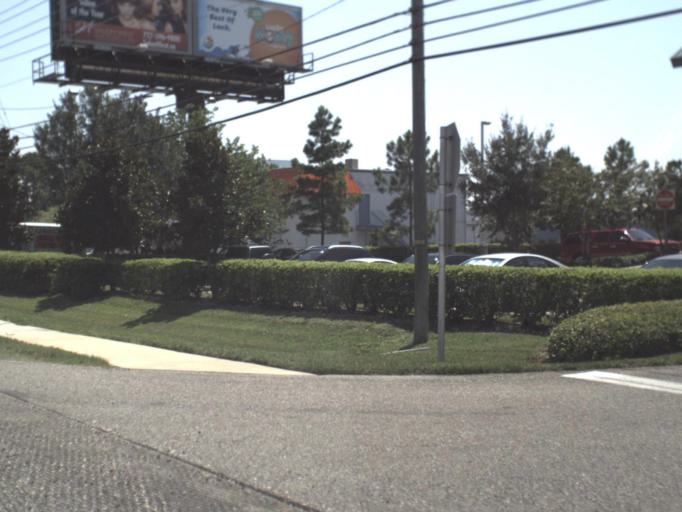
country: US
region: Florida
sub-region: Pinellas County
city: Saint George
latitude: 28.0429
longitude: -82.7385
